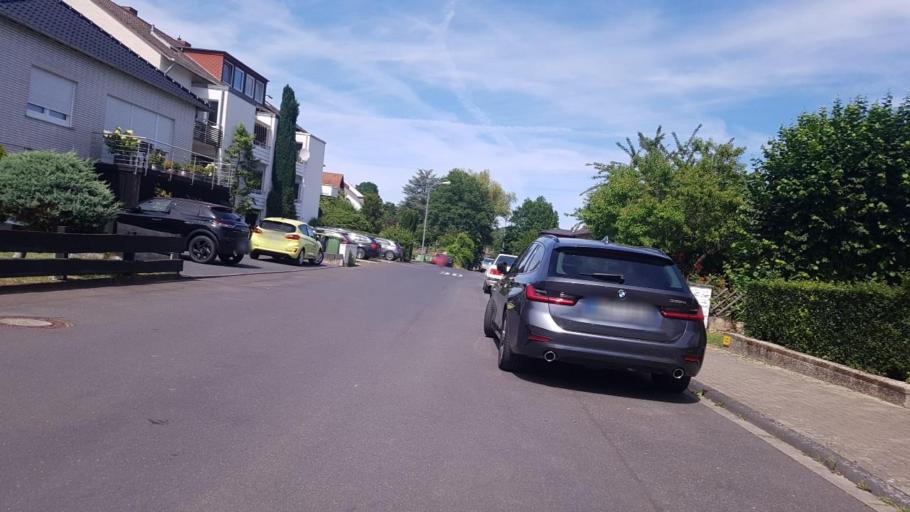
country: DE
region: North Rhine-Westphalia
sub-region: Regierungsbezirk Koln
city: Konigswinter
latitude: 50.6415
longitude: 7.1732
